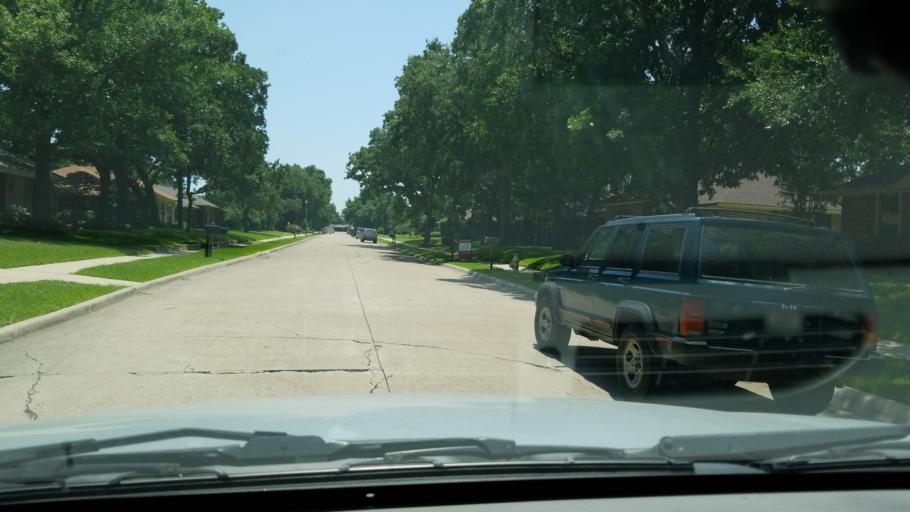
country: US
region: Texas
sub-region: Dallas County
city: Coppell
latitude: 32.9688
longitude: -96.9864
